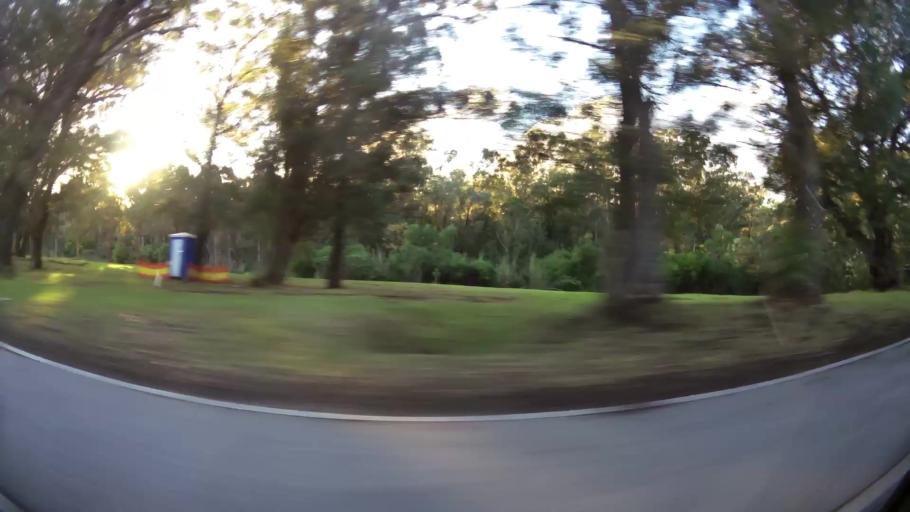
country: ZA
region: Eastern Cape
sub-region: Nelson Mandela Bay Metropolitan Municipality
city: Port Elizabeth
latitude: -33.9598
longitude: 25.5130
